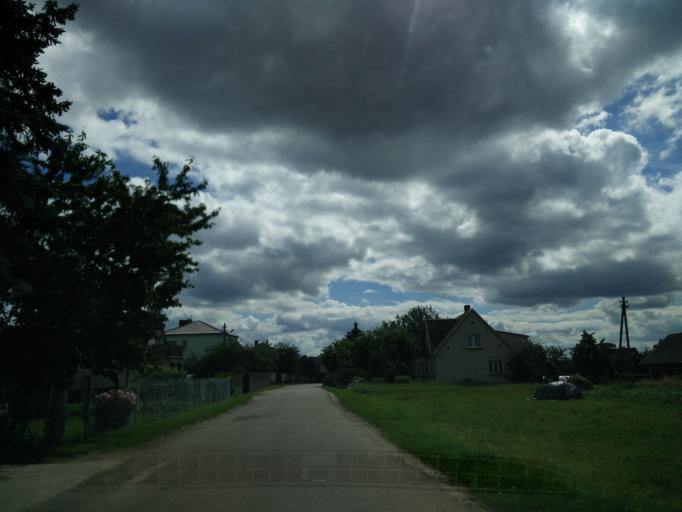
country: LT
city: Trakai
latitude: 54.6101
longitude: 24.9865
